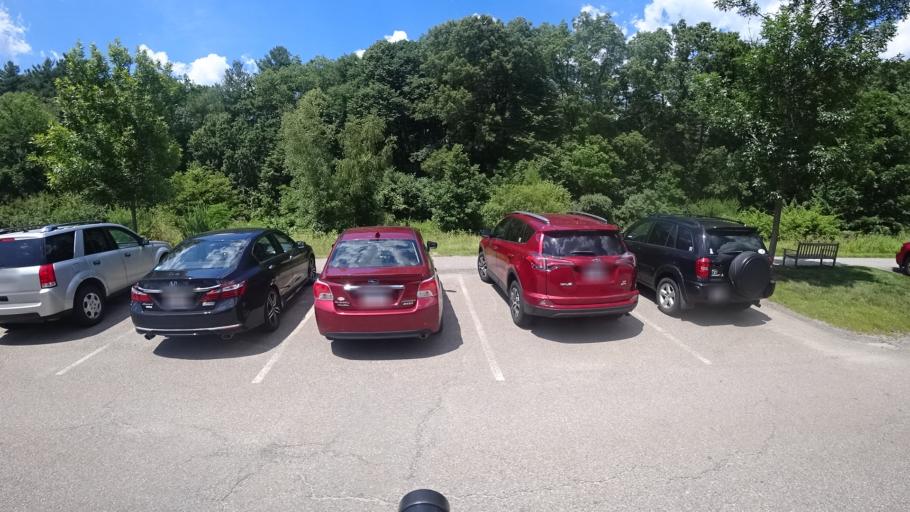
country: US
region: Massachusetts
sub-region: Norfolk County
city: Dedham
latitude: 42.2677
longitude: -71.1947
